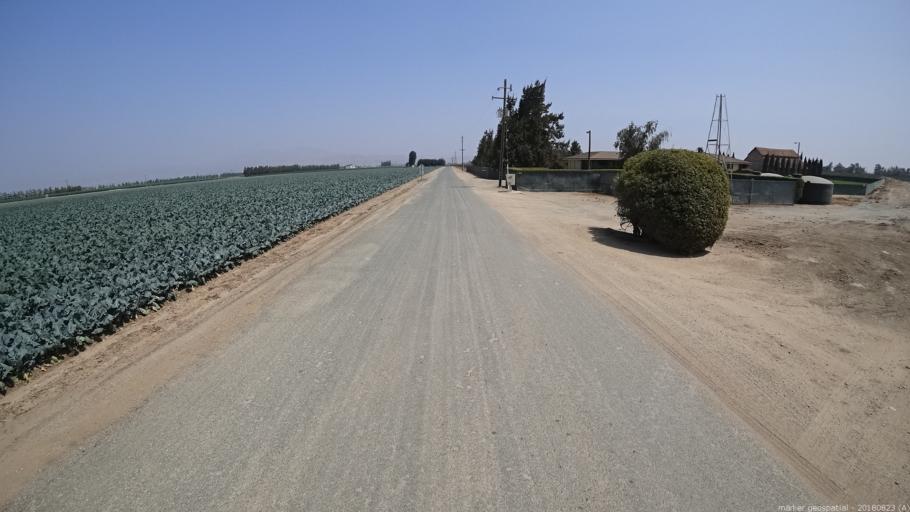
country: US
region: California
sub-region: Monterey County
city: Greenfield
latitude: 36.3189
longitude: -121.2806
